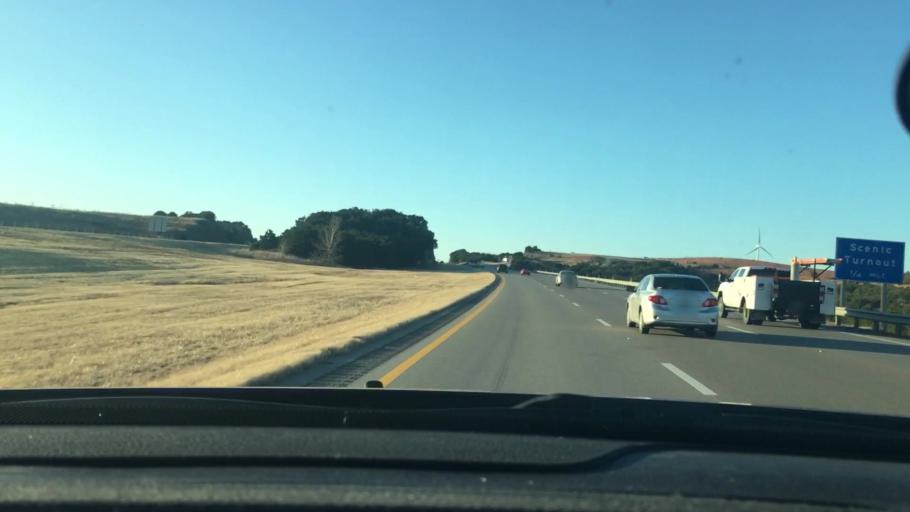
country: US
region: Oklahoma
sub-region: Murray County
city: Davis
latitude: 34.4315
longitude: -97.1319
